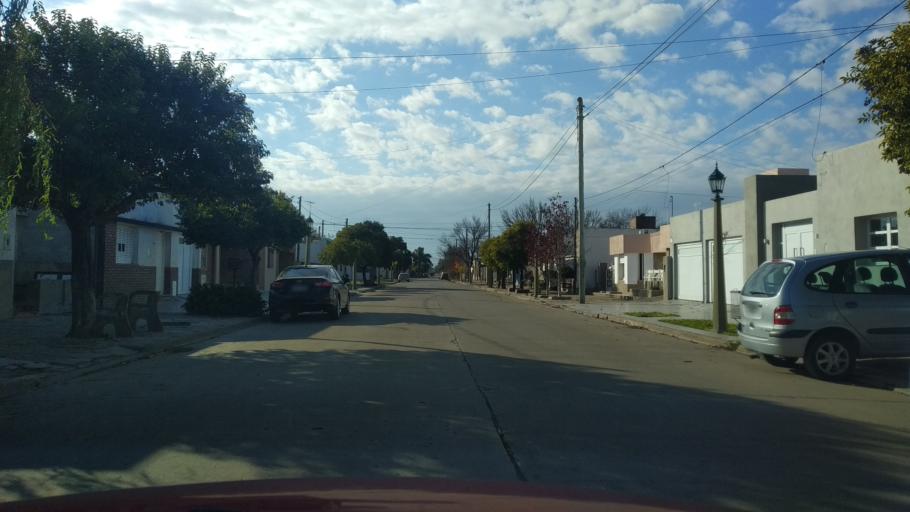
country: AR
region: Cordoba
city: Leones
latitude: -32.6580
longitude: -62.3005
